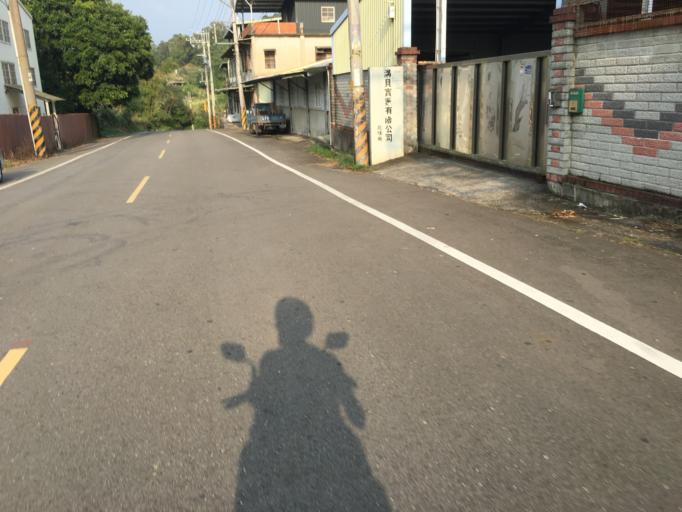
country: TW
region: Taiwan
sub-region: Hsinchu
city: Hsinchu
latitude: 24.7050
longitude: 121.0540
